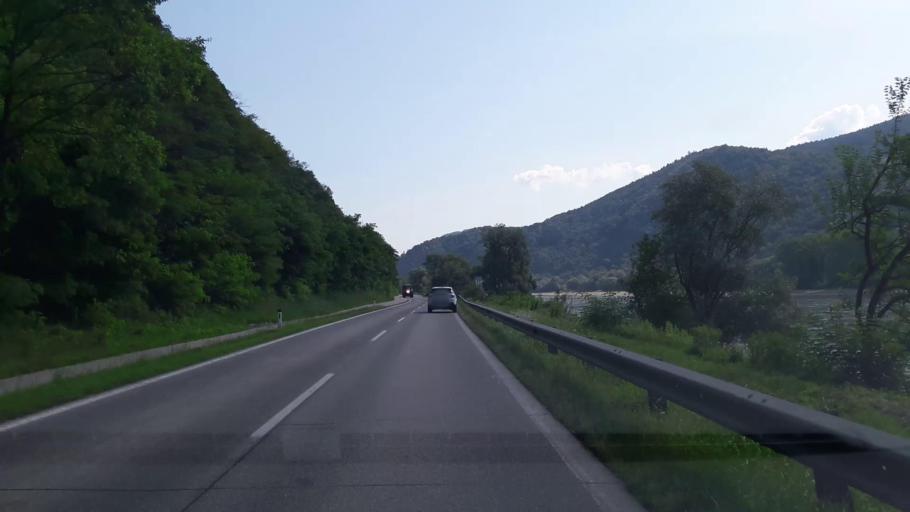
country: AT
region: Lower Austria
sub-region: Politischer Bezirk Krems
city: Aggsbach
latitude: 48.2767
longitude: 15.3861
